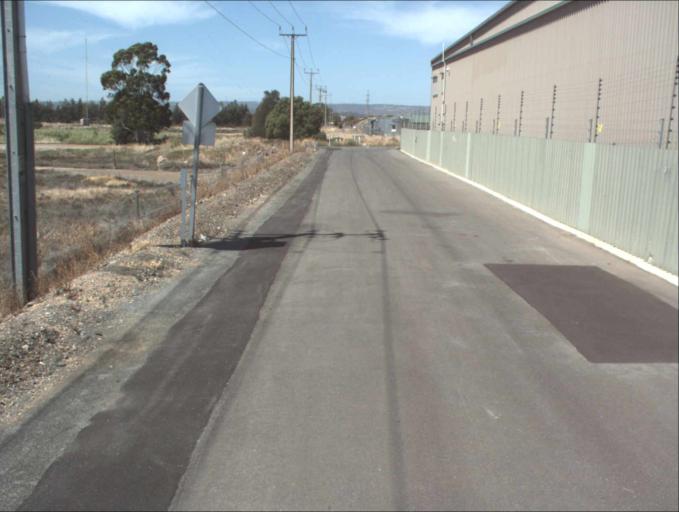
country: AU
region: South Australia
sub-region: Port Adelaide Enfield
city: Blair Athol
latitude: -34.8384
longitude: 138.5717
